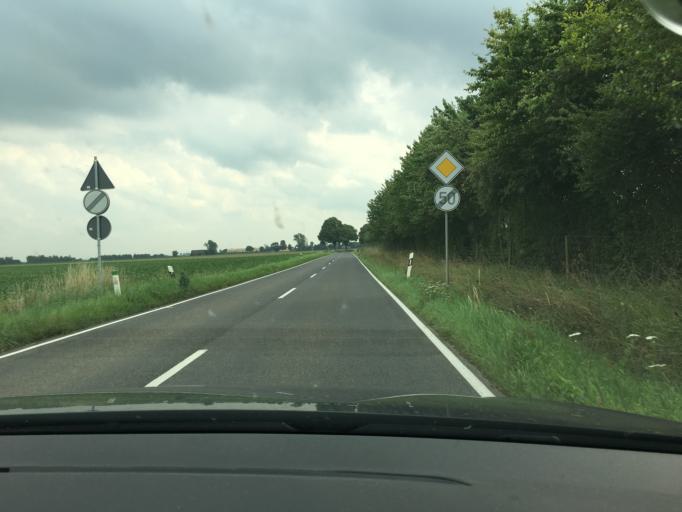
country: DE
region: North Rhine-Westphalia
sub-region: Regierungsbezirk Koln
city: Vettweiss
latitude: 50.7723
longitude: 6.5531
